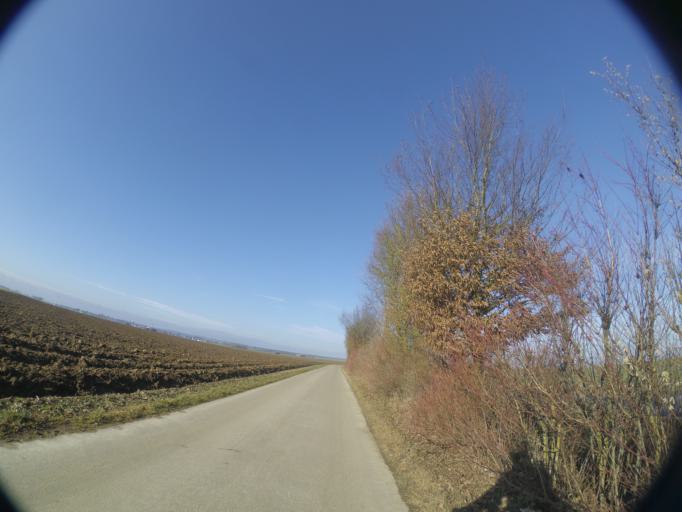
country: DE
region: Baden-Wuerttemberg
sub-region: Tuebingen Region
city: Dornstadt
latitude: 48.4775
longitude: 9.9355
